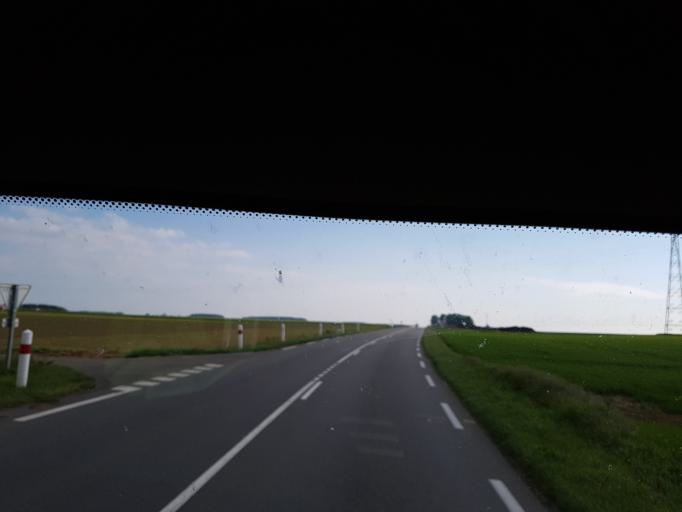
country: FR
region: Picardie
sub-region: Departement de la Somme
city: Crecy-en-Ponthieu
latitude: 50.2483
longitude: 1.9619
